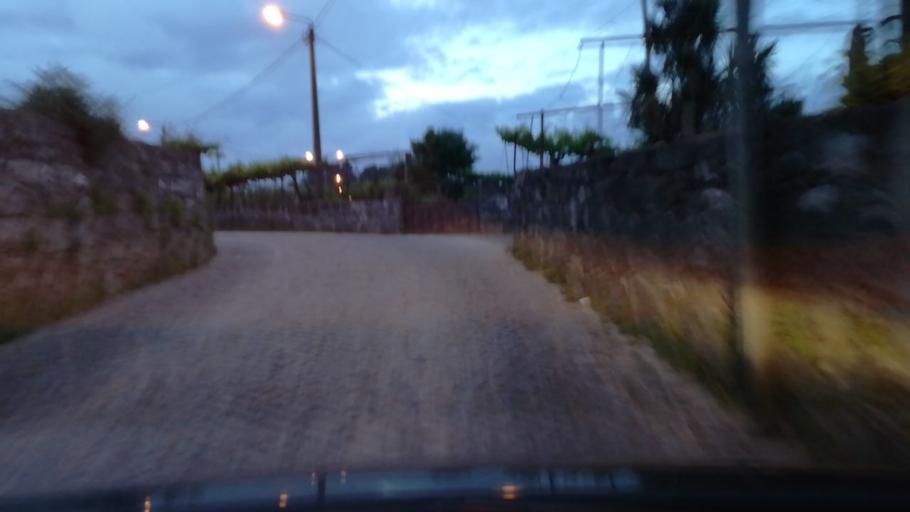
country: PT
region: Porto
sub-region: Maia
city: Maia
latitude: 41.2542
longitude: -8.6083
